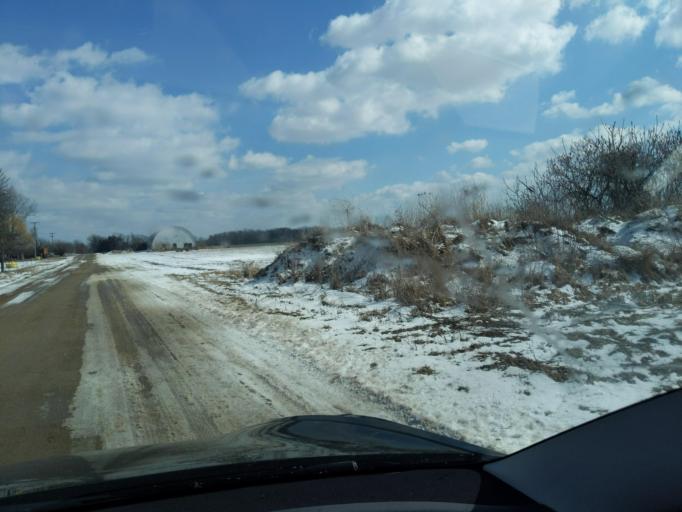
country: US
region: Michigan
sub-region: Livingston County
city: Fowlerville
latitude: 42.6139
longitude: -84.1040
